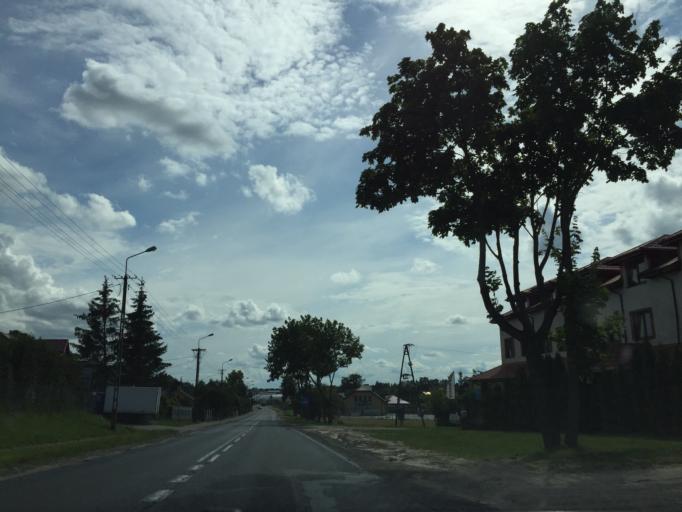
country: PL
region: Masovian Voivodeship
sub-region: Powiat losicki
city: Losice
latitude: 52.2137
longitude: 22.7293
